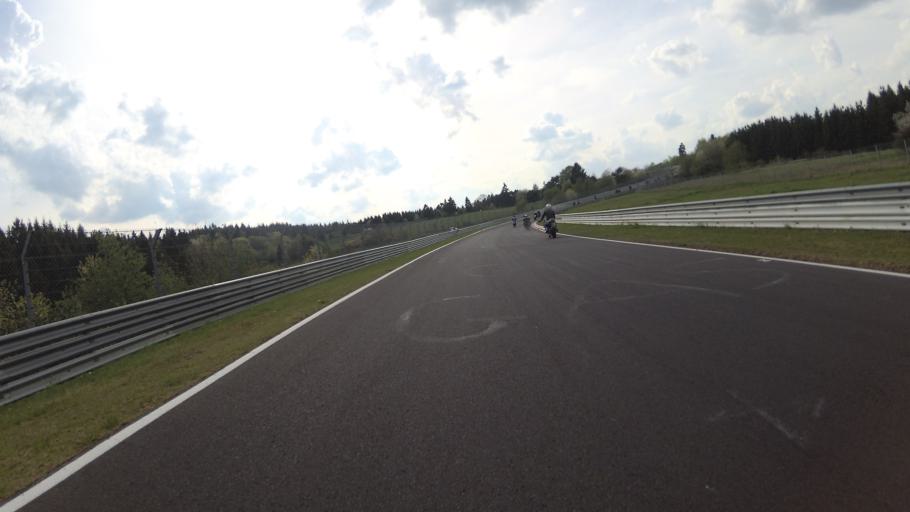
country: DE
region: Rheinland-Pfalz
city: Drees
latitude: 50.3581
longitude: 6.9871
